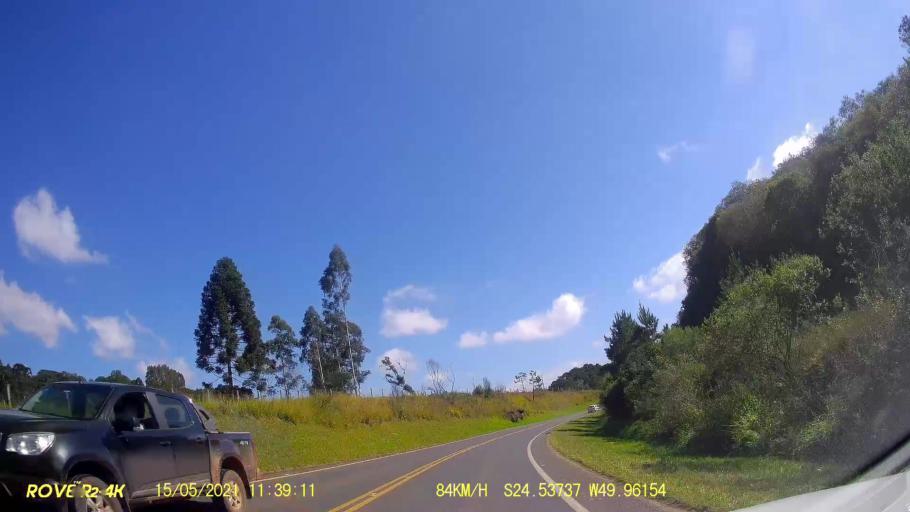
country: BR
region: Parana
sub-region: Pirai Do Sul
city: Pirai do Sul
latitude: -24.5363
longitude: -49.9621
